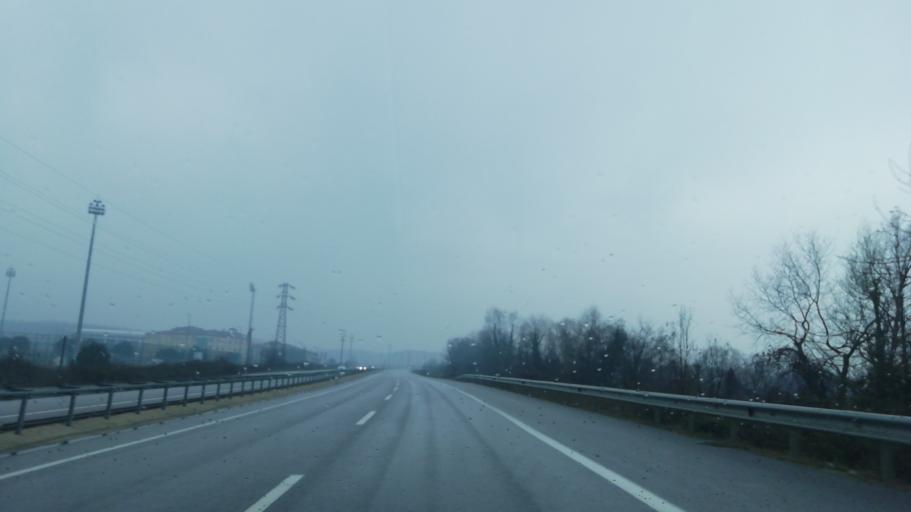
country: TR
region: Sakarya
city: Akyazi
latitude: 40.6687
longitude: 30.5899
